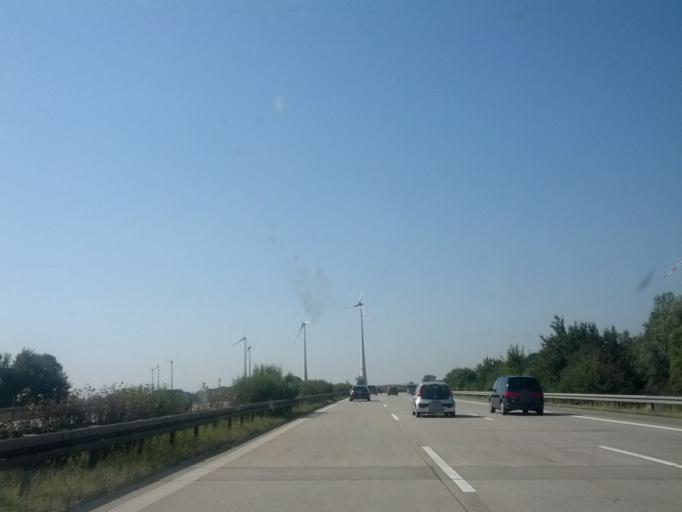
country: DE
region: Brandenburg
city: Borkheide
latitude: 52.1798
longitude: 12.8398
